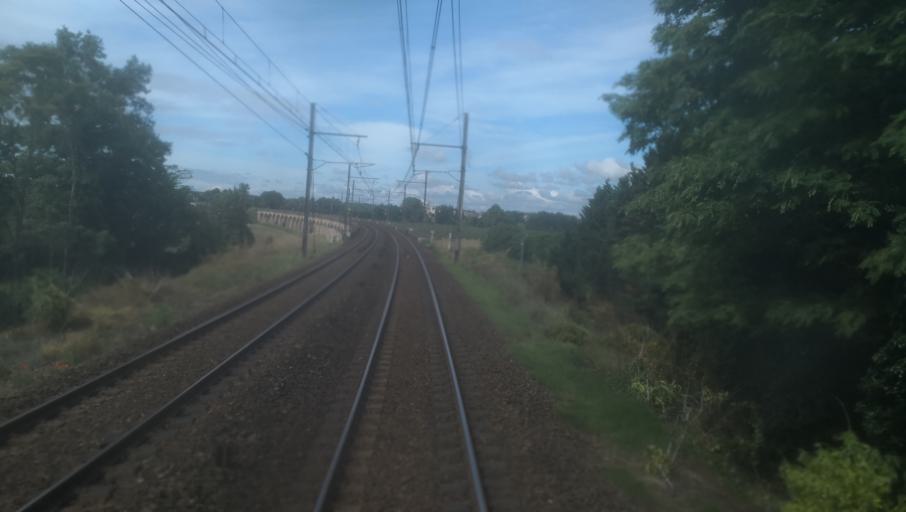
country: FR
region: Aquitaine
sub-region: Departement de la Gironde
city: Langon
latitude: 44.5647
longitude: -0.2430
